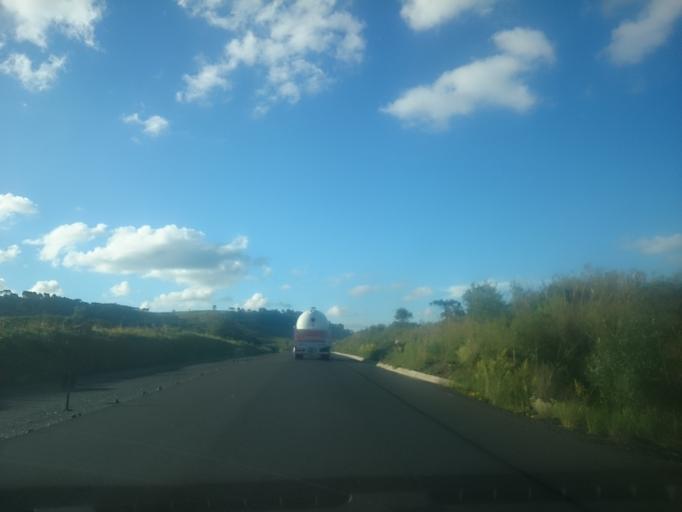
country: BR
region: Santa Catarina
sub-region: Sao Joaquim
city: Sao Joaquim
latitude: -28.0743
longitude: -50.0724
